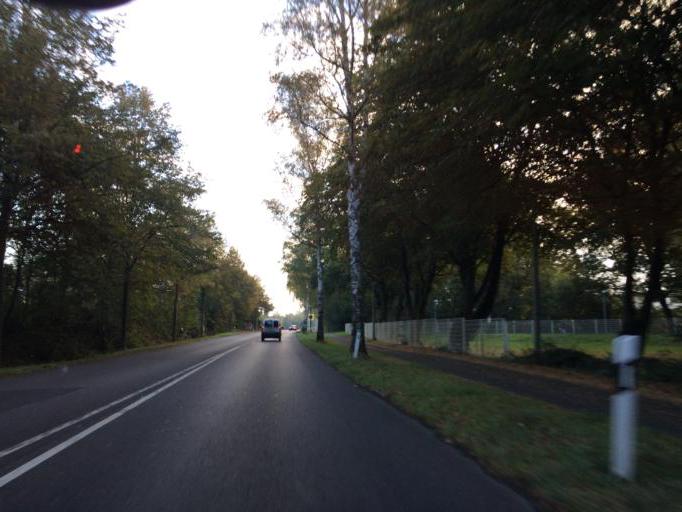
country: DE
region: North Rhine-Westphalia
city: Sankt Augustin
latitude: 50.7563
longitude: 7.1662
